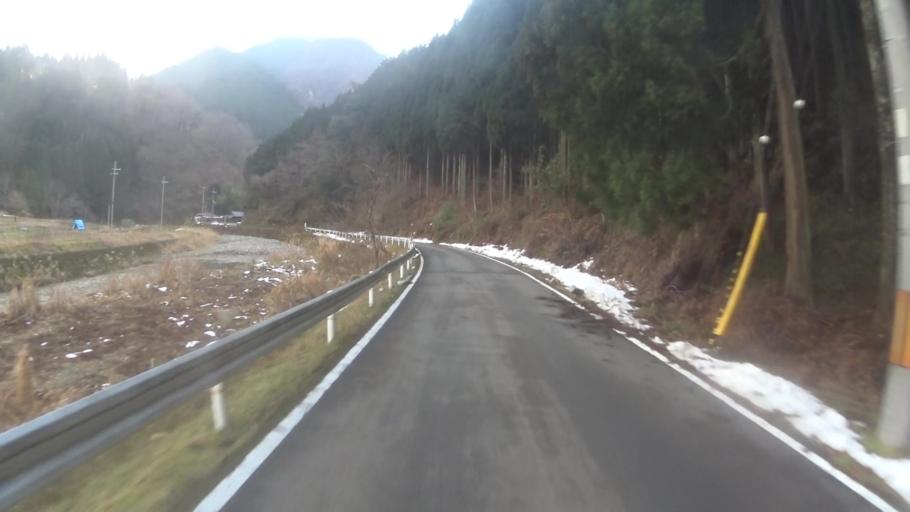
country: JP
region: Kyoto
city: Maizuru
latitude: 35.3894
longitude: 135.4716
